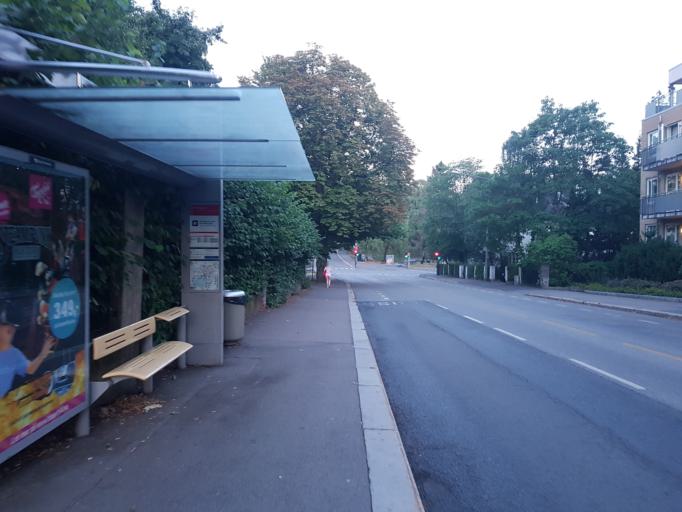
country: NO
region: Oslo
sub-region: Oslo
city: Oslo
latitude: 59.9307
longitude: 10.7430
